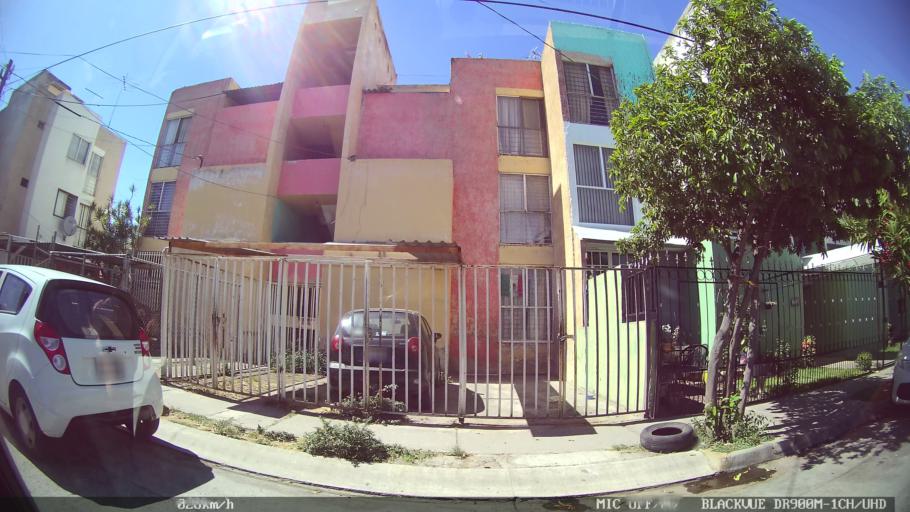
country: MX
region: Jalisco
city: Tlaquepaque
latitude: 20.6452
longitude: -103.2890
